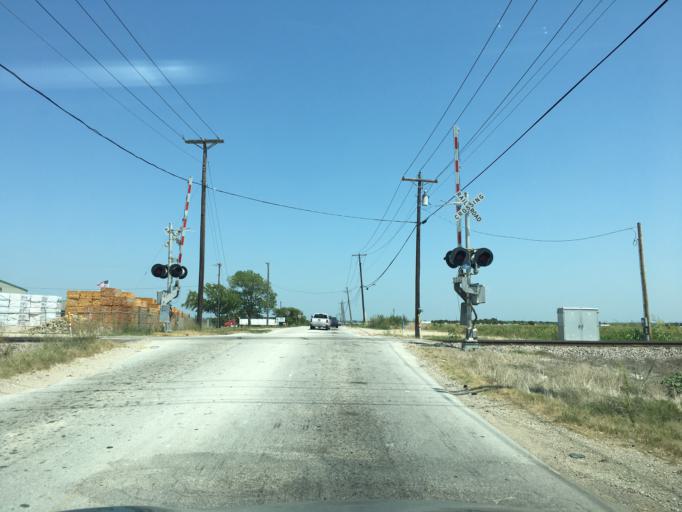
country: US
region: Texas
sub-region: Tarrant County
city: Edgecliff Village
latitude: 32.6140
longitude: -97.3317
